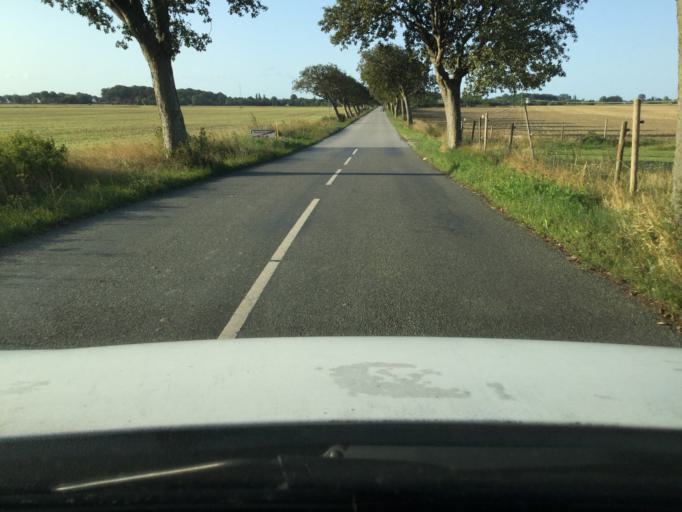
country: DK
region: Zealand
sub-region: Lolland Kommune
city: Rodby
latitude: 54.7081
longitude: 11.3886
